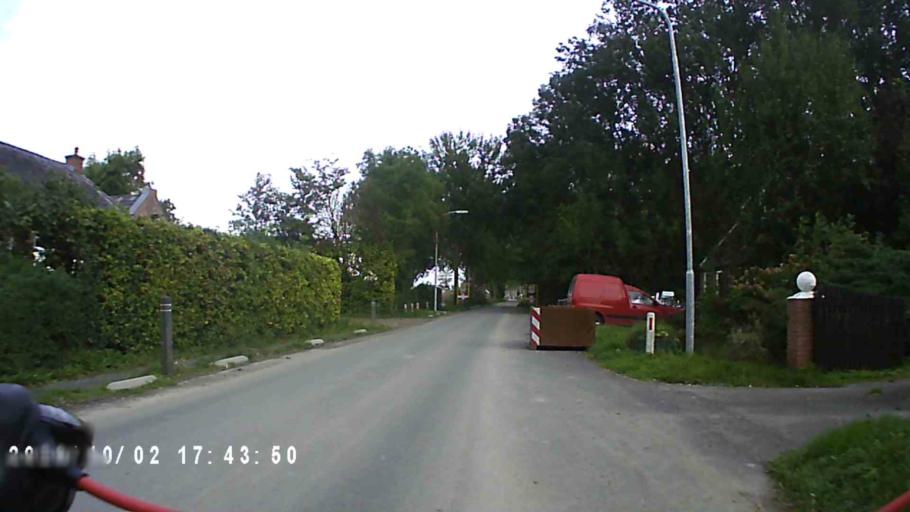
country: NL
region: Groningen
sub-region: Gemeente Zuidhorn
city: Oldehove
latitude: 53.3358
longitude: 6.3843
